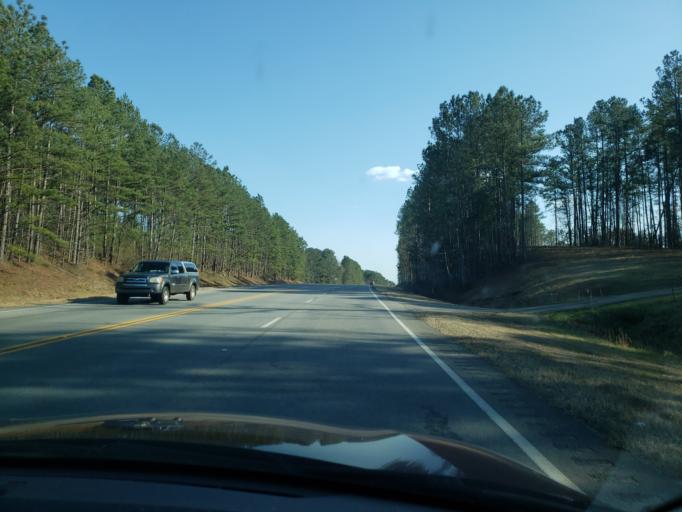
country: US
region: Alabama
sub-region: Randolph County
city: Wedowee
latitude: 33.4647
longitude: -85.5756
